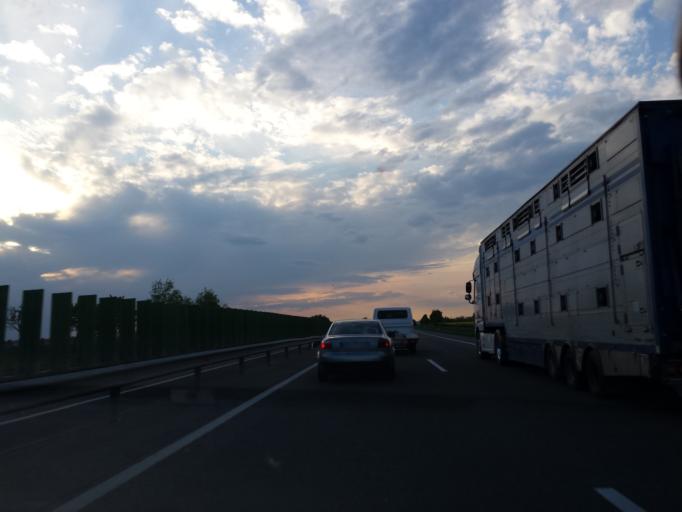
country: HU
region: Gyor-Moson-Sopron
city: Mosonszentmiklos
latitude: 47.7280
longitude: 17.4498
